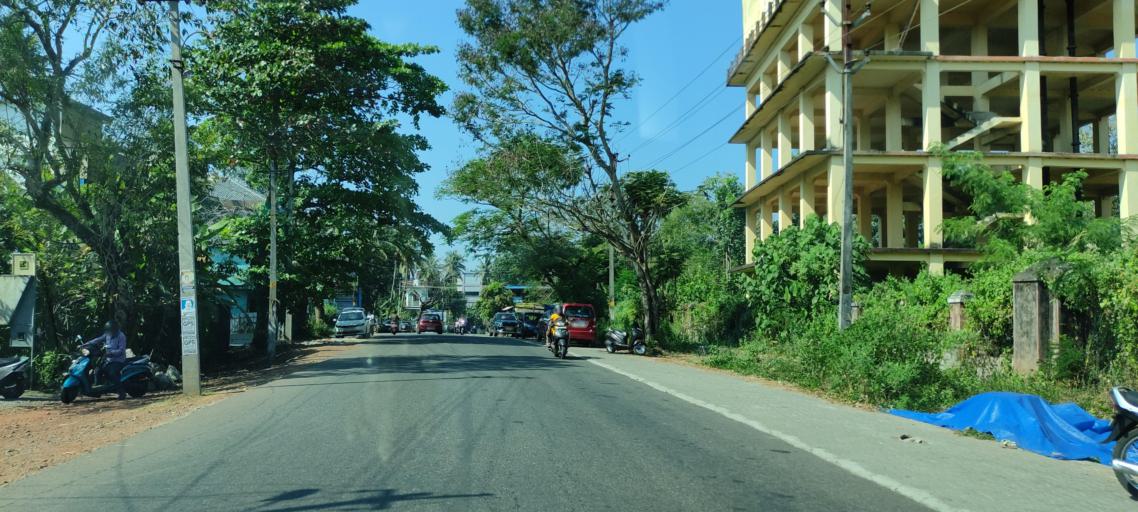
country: IN
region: Kerala
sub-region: Kollam
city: Panmana
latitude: 9.0439
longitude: 76.6223
